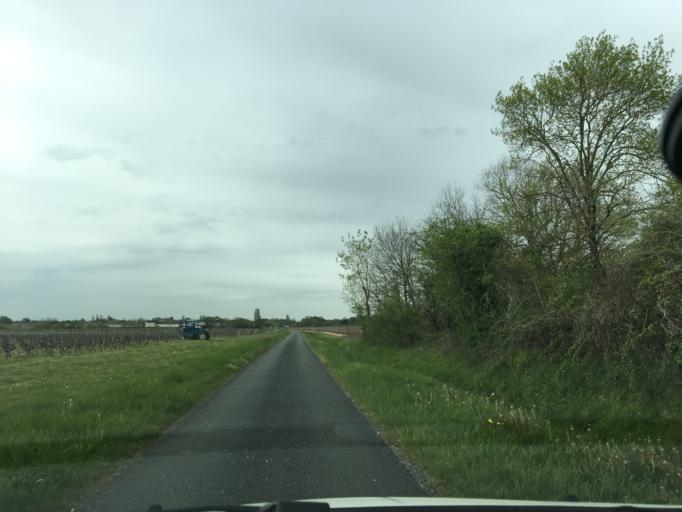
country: FR
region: Aquitaine
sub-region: Departement de la Gironde
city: Lesparre-Medoc
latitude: 45.3223
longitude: -0.8953
